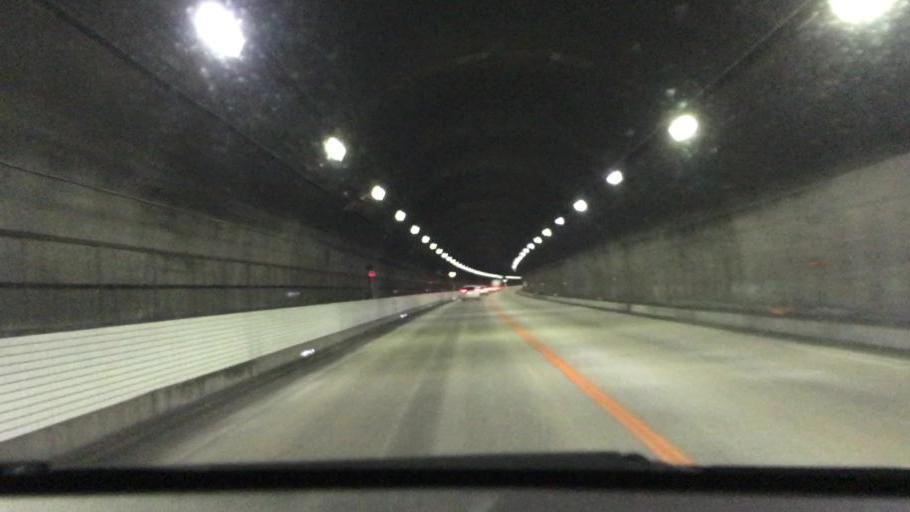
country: JP
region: Yamaguchi
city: Tokuyama
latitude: 34.0867
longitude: 131.7475
